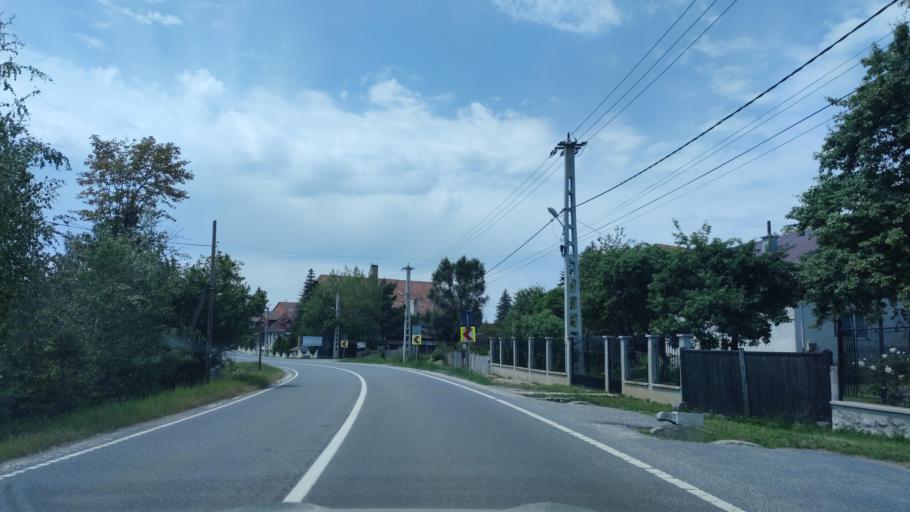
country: RO
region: Harghita
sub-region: Comuna Sandominic
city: Sandominic
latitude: 46.6239
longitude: 25.7172
